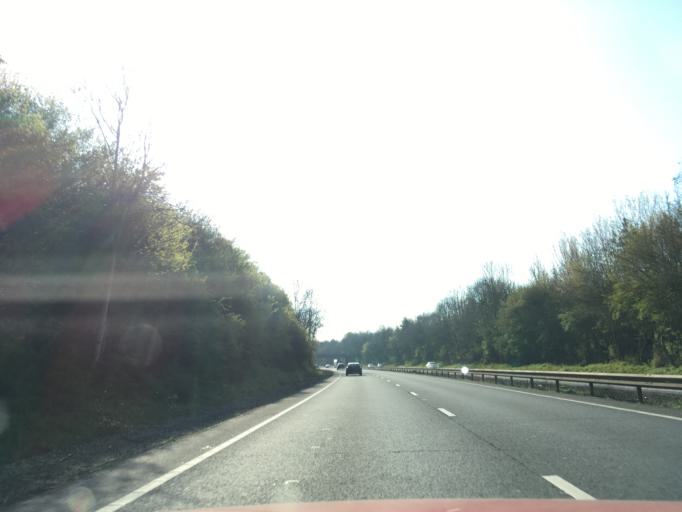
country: GB
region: England
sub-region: Milton Keynes
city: Stony Stratford
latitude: 52.0531
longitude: -0.8327
